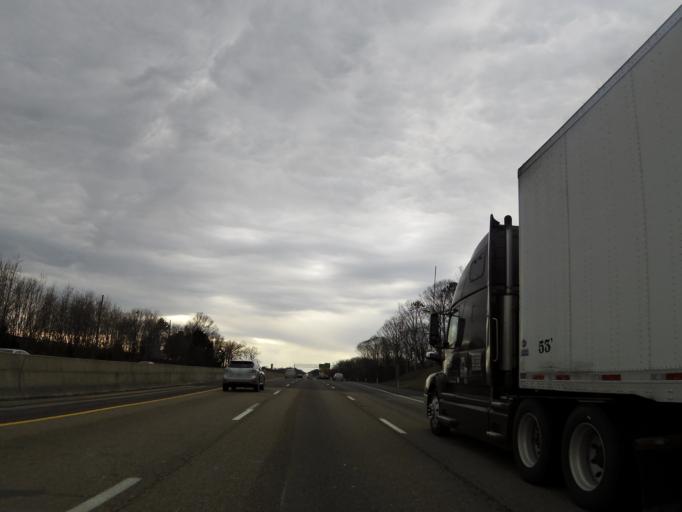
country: US
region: Tennessee
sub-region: Knox County
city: Farragut
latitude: 35.9019
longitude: -84.1627
